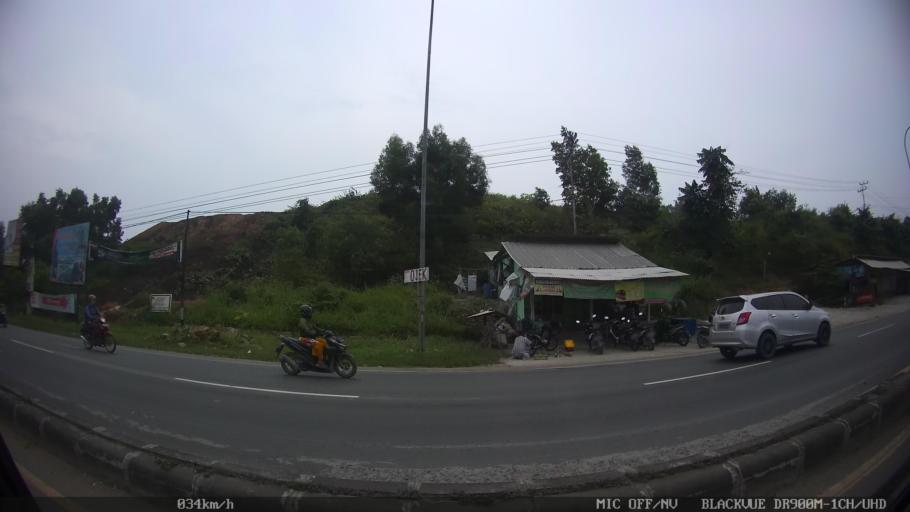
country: ID
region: Lampung
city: Panjang
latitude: -5.4084
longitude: 105.3481
